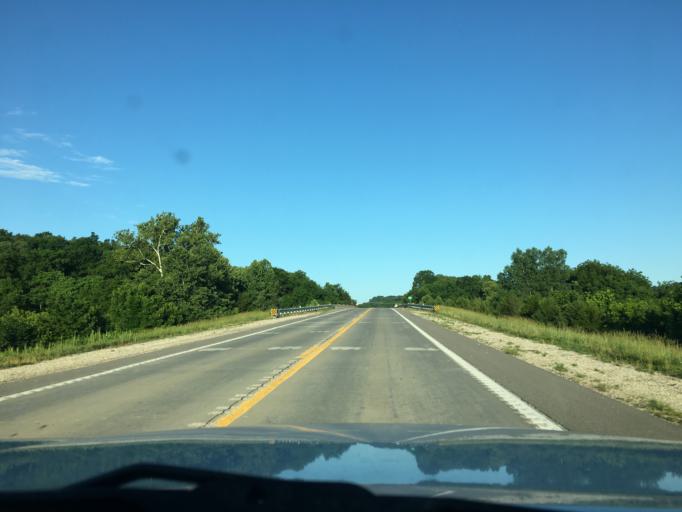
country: US
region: Missouri
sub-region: Gasconade County
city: Owensville
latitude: 38.4849
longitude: -91.5435
